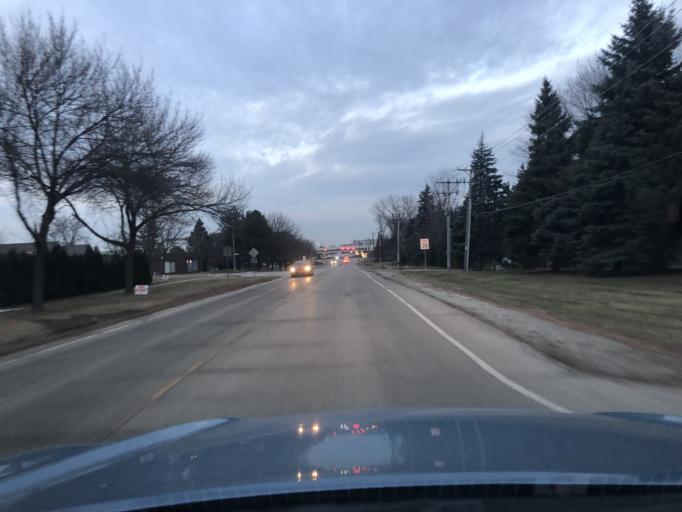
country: US
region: Illinois
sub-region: DuPage County
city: Itasca
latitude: 41.9801
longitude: -88.0054
